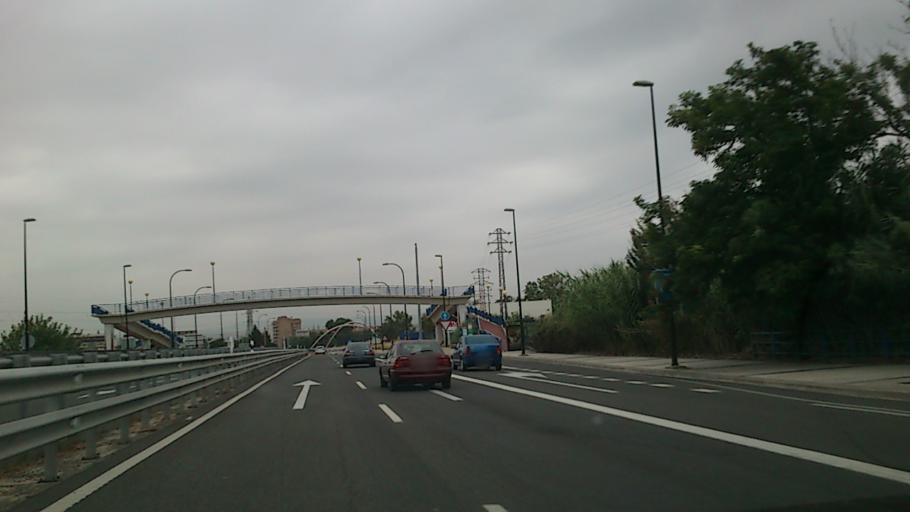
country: ES
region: Aragon
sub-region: Provincia de Zaragoza
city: Zaragoza
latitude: 41.6942
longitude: -0.8697
